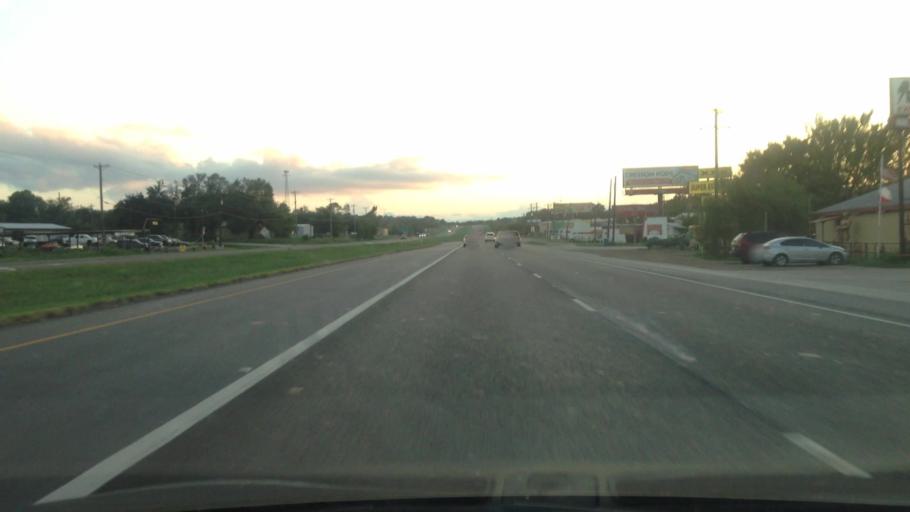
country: US
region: Texas
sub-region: Tarrant County
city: Benbrook
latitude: 32.6166
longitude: -97.5359
